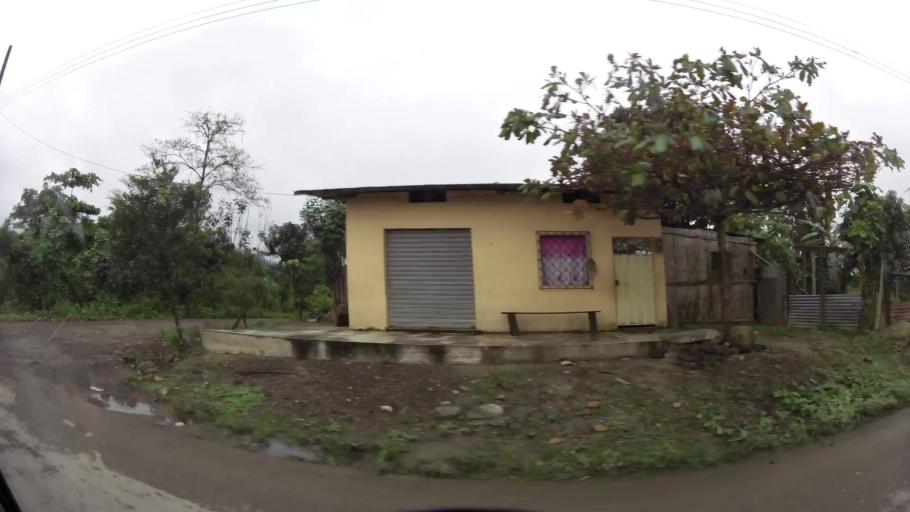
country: EC
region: El Oro
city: Pasaje
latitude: -3.3290
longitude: -79.7789
